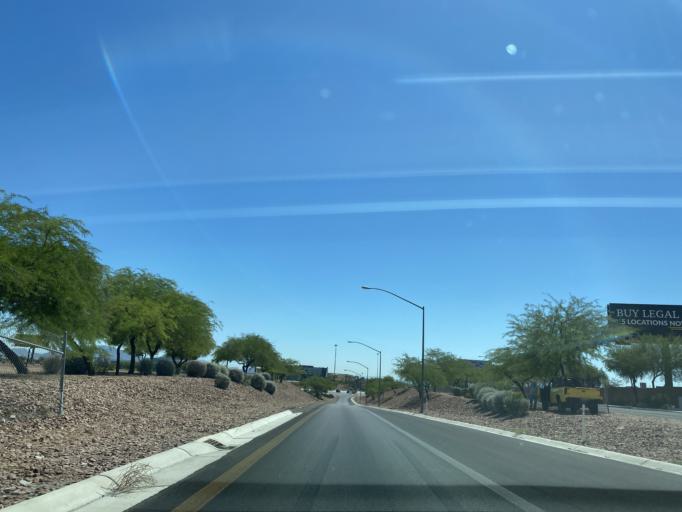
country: US
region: Nevada
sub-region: Clark County
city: Paradise
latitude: 36.0627
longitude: -115.1706
